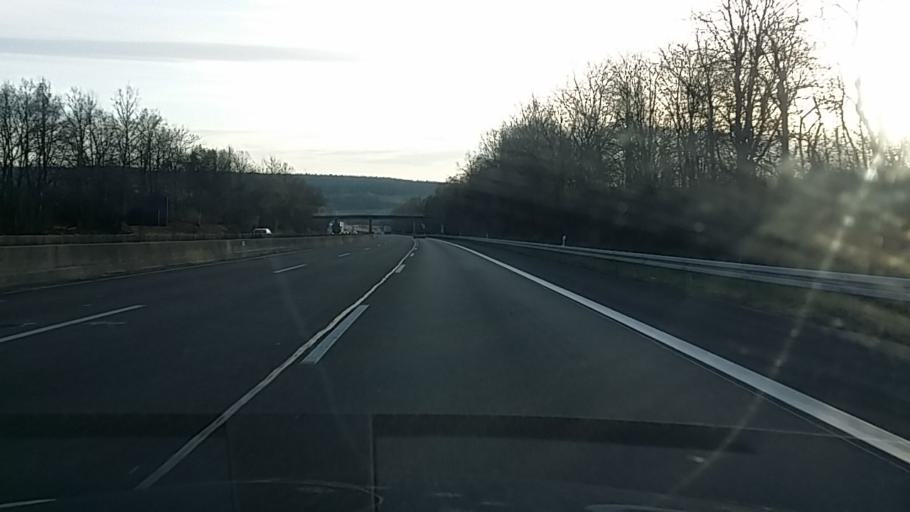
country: DE
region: Hesse
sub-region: Regierungsbezirk Kassel
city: Burghaun
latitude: 50.6695
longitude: 9.6769
